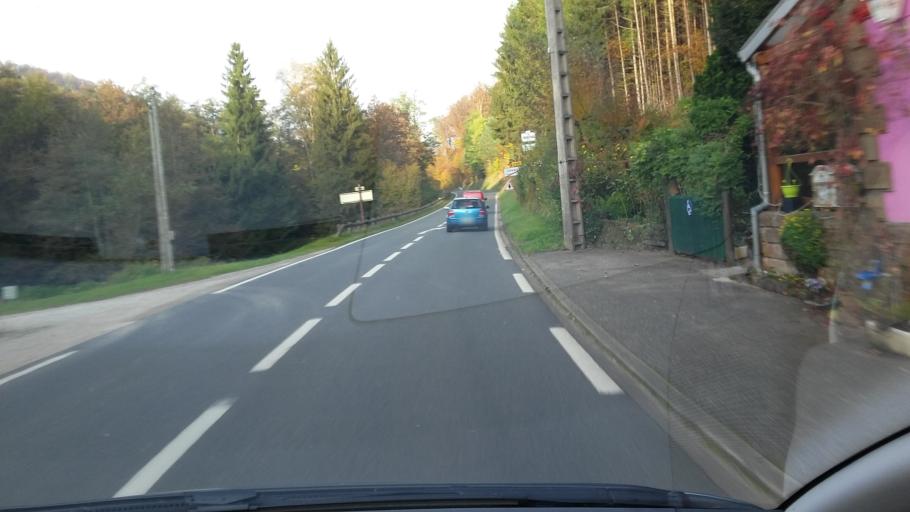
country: FR
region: Lorraine
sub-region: Departement de la Moselle
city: Dabo
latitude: 48.7083
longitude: 7.2157
